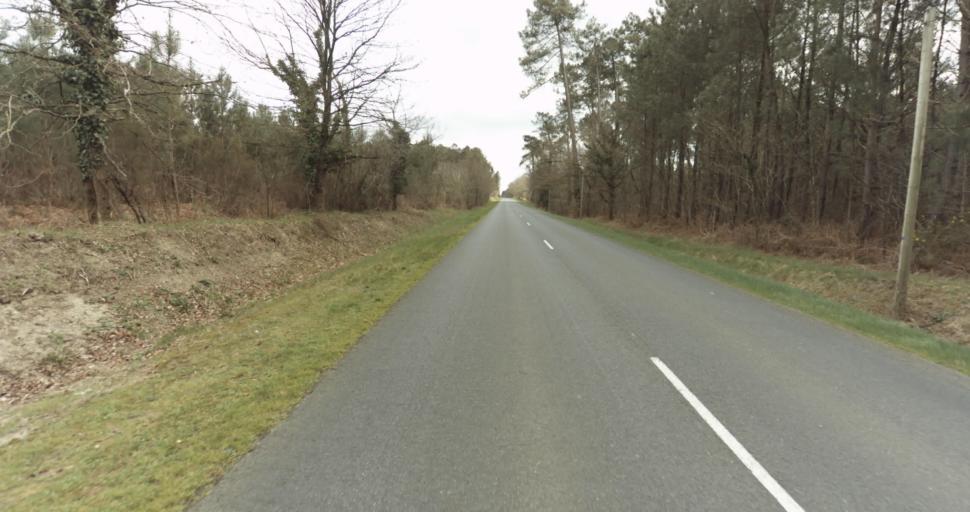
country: FR
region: Aquitaine
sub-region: Departement des Landes
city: Roquefort
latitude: 44.0540
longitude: -0.3824
